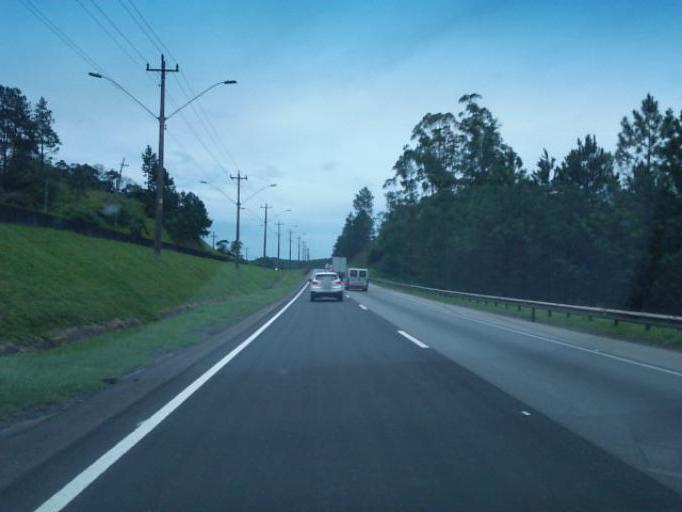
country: BR
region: Sao Paulo
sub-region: Sao Lourenco Da Serra
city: Sao Lourenco da Serra
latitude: -23.8697
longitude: -46.9580
